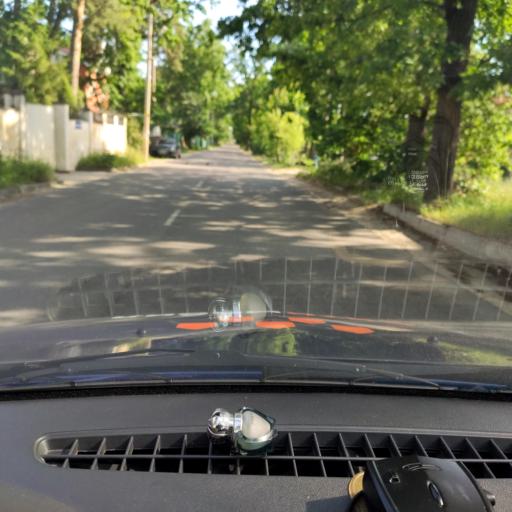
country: RU
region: Voronezj
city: Somovo
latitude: 51.7479
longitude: 39.3661
